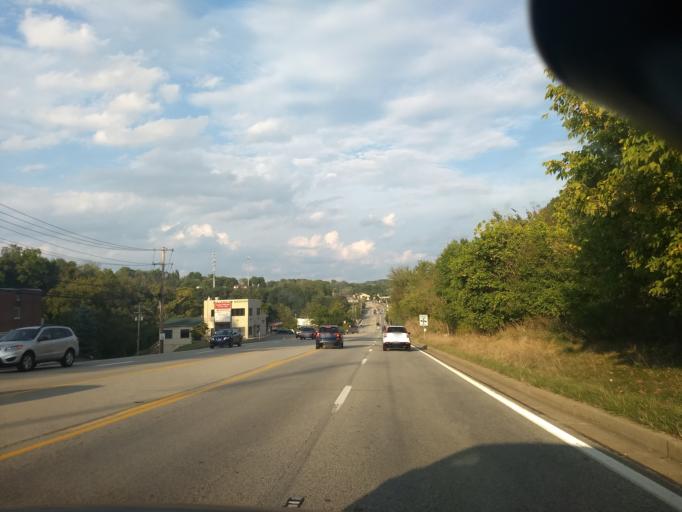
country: US
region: Pennsylvania
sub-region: Washington County
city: Thompsonville
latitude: 40.2898
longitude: -80.1111
